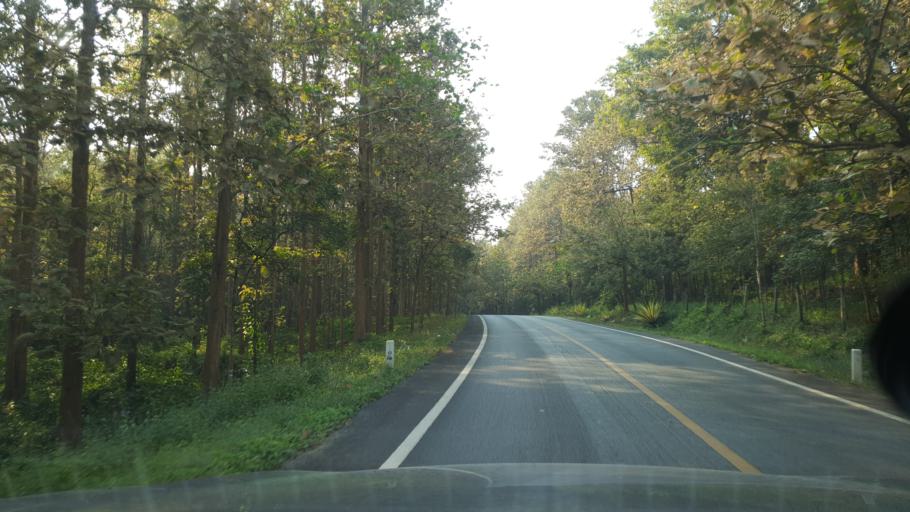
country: TH
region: Chiang Mai
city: Mae On
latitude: 18.6859
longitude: 99.2987
